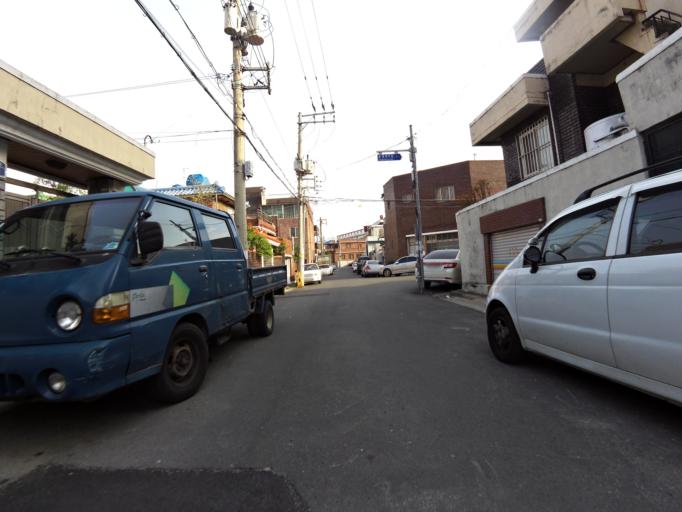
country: KR
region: Daegu
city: Daegu
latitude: 35.8710
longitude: 128.6471
